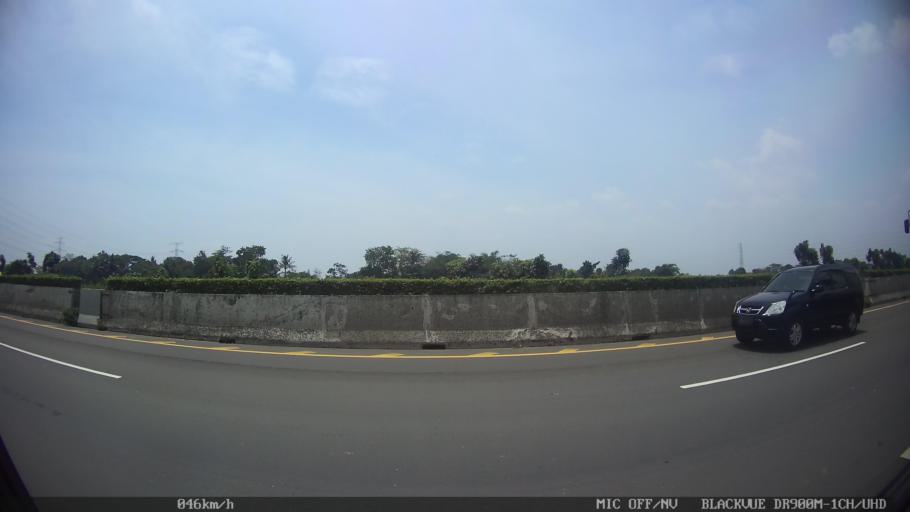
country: ID
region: West Java
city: Kresek
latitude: -6.1931
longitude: 106.4216
